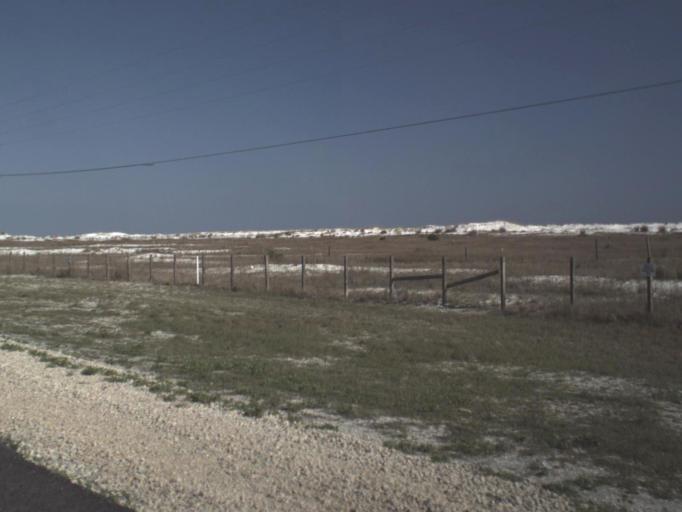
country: US
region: Florida
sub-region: Okaloosa County
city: Lake Lorraine
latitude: 30.3941
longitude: -86.5562
